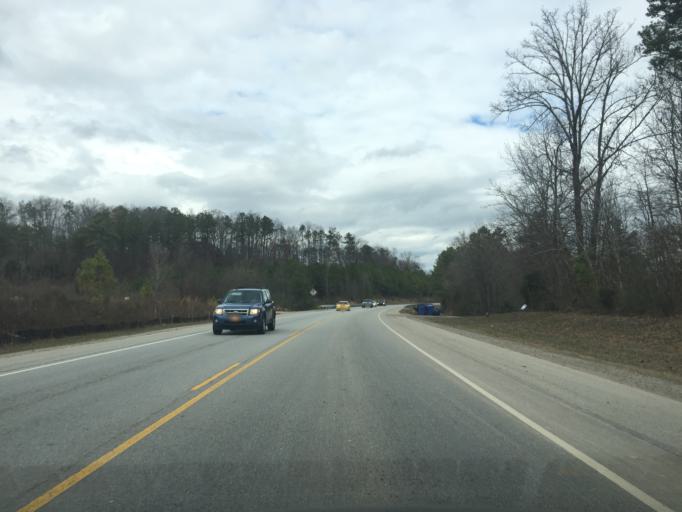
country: US
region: Tennessee
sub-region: Hamilton County
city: Collegedale
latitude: 35.0709
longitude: -85.0730
